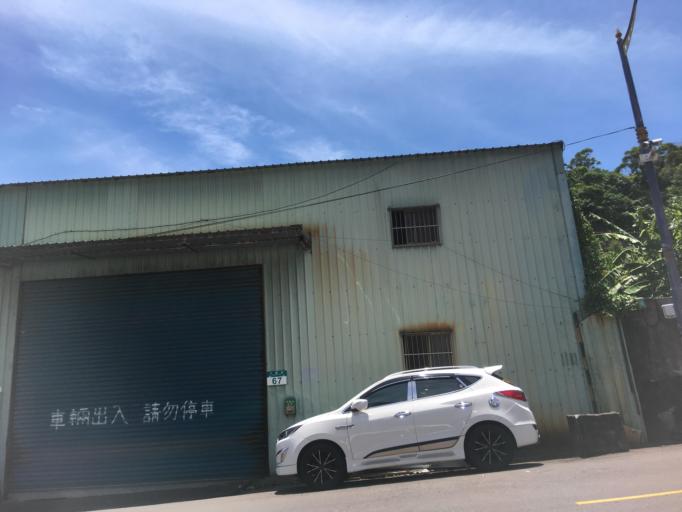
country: TW
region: Taipei
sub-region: Taipei
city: Banqiao
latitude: 25.0554
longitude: 121.4264
